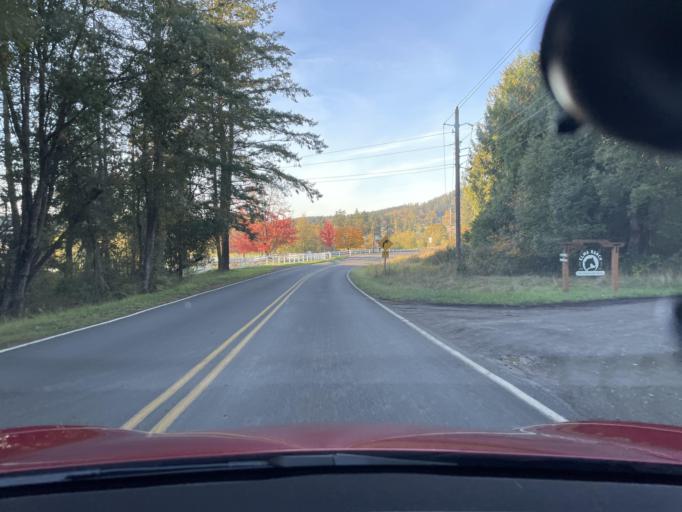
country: US
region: Washington
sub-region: San Juan County
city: Friday Harbor
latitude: 48.5649
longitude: -123.1417
